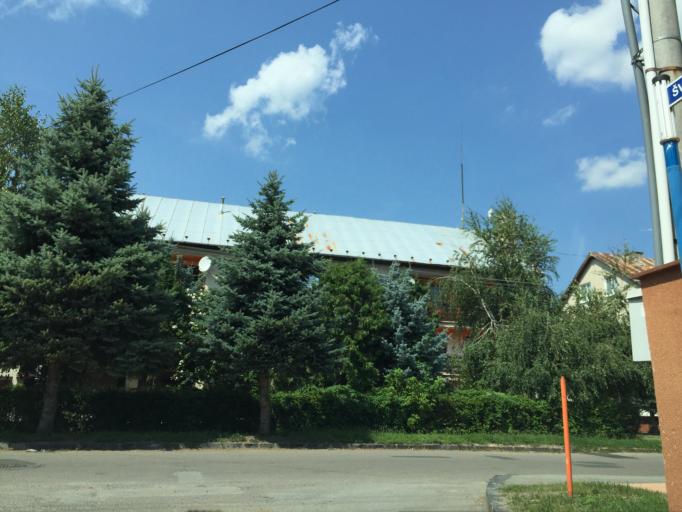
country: SK
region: Kosicky
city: Sobrance
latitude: 48.7425
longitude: 22.1843
